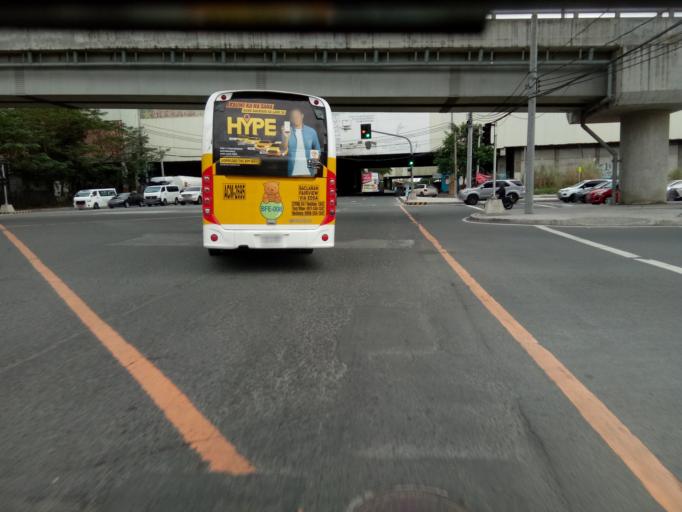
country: PH
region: Metro Manila
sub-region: Makati City
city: Makati City
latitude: 14.5175
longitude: 120.9905
